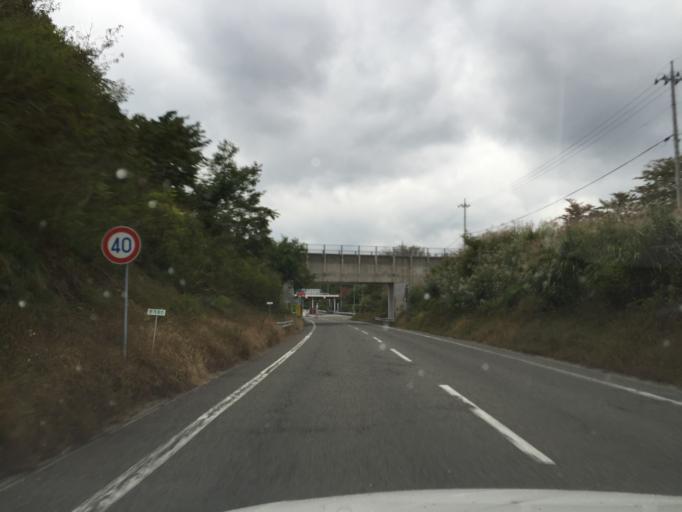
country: JP
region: Fukushima
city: Miharu
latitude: 37.4441
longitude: 140.5258
